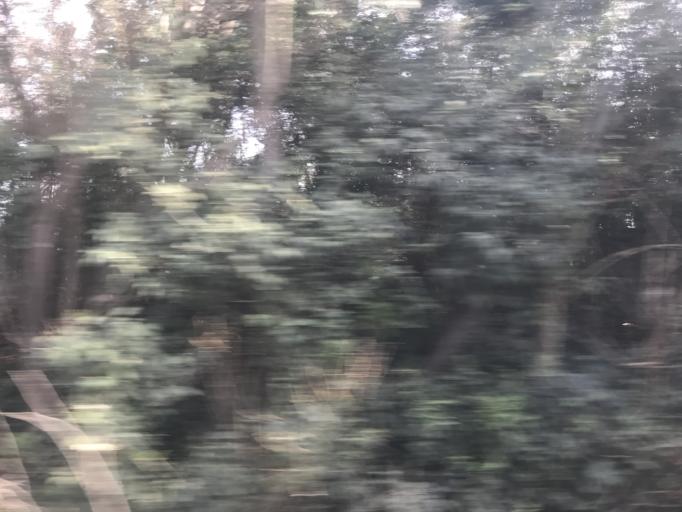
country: AR
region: Cordoba
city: Laguna Larga
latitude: -31.7883
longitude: -63.7933
